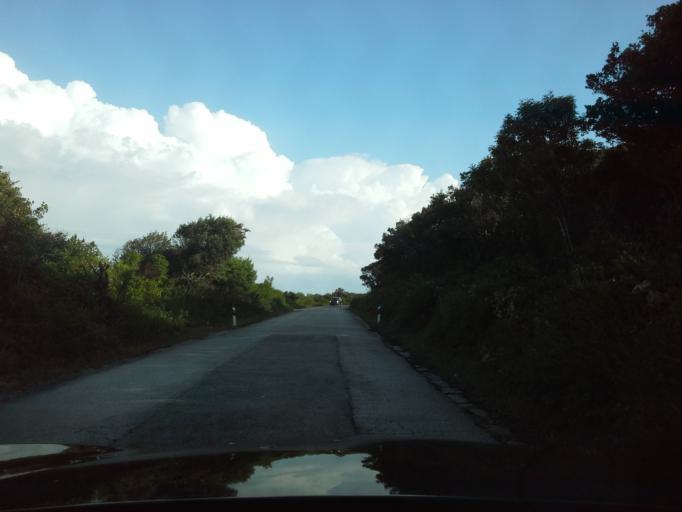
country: HR
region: Primorsko-Goranska
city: Mali Losinj
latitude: 44.6876
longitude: 14.3931
